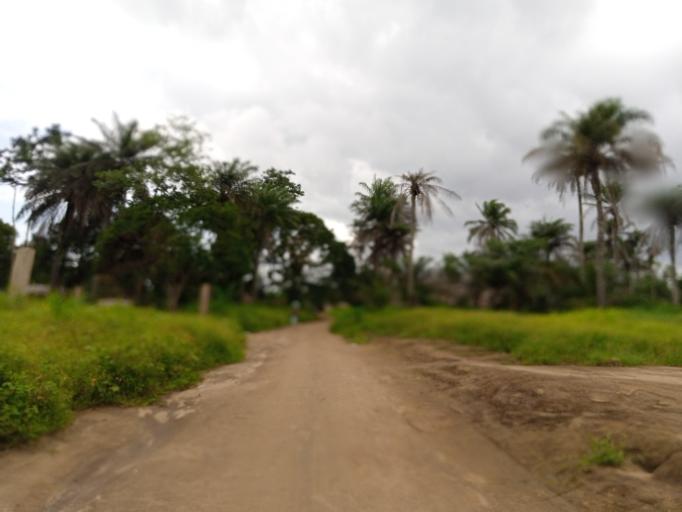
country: SL
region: Northern Province
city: Masoyila
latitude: 8.5777
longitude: -13.1627
